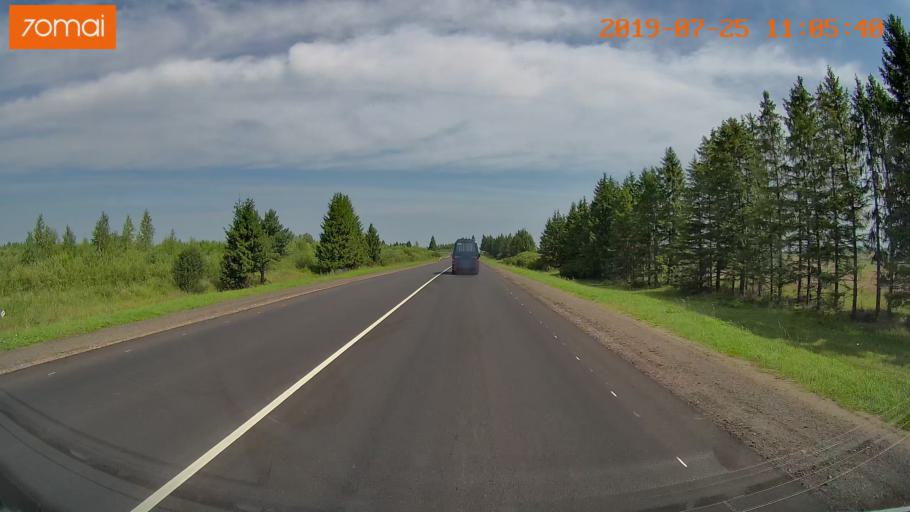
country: RU
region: Ivanovo
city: Furmanov
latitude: 57.2453
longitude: 41.1521
